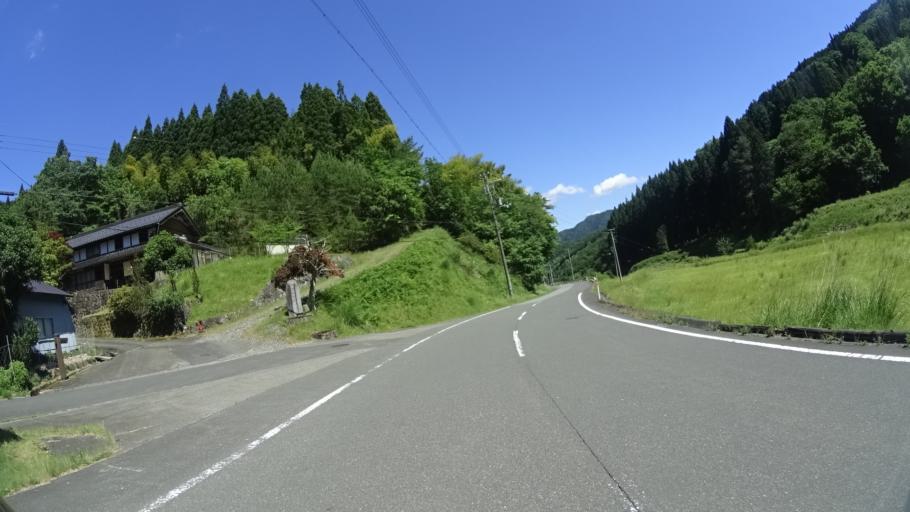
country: JP
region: Kyoto
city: Fukuchiyama
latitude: 35.4306
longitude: 135.0493
